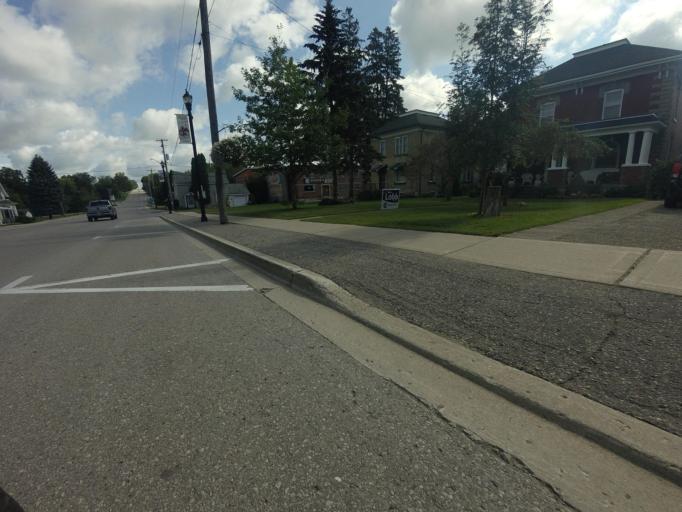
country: CA
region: Ontario
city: Huron East
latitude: 43.7380
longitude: -81.4281
